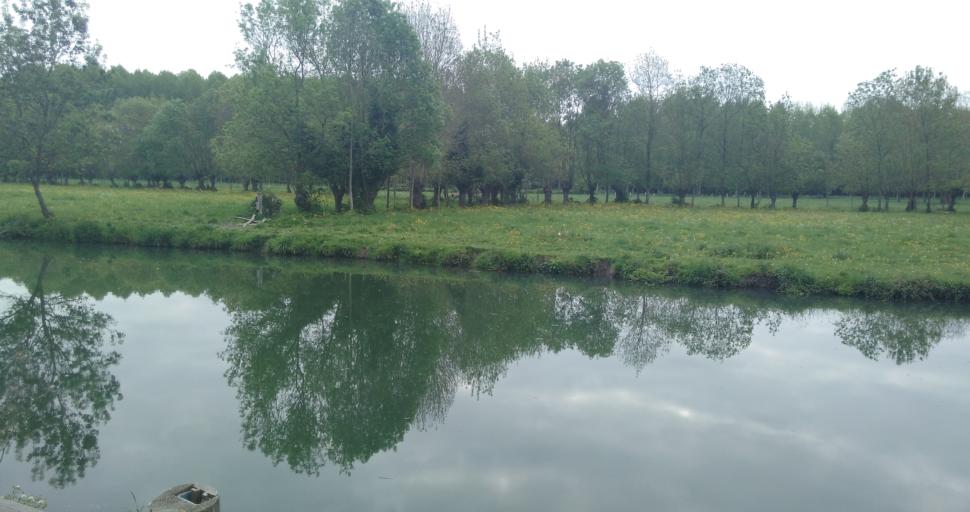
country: FR
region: Poitou-Charentes
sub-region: Departement des Deux-Sevres
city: Coulon
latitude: 46.3134
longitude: -0.6100
